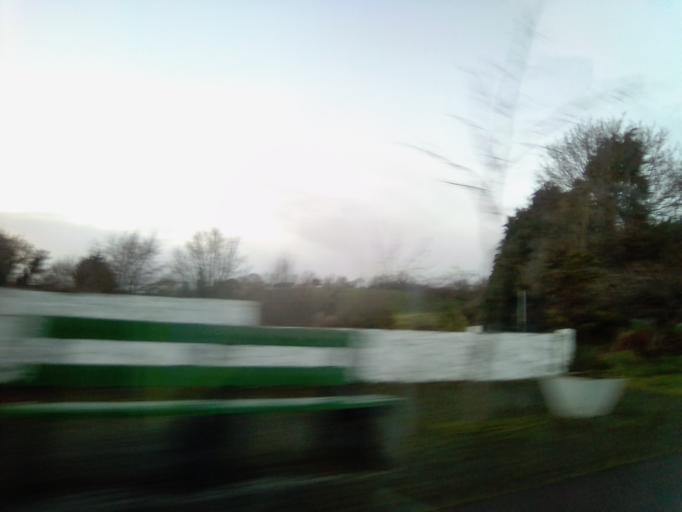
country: IE
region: Ulster
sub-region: County Monaghan
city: Monaghan
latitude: 54.3430
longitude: -6.9588
